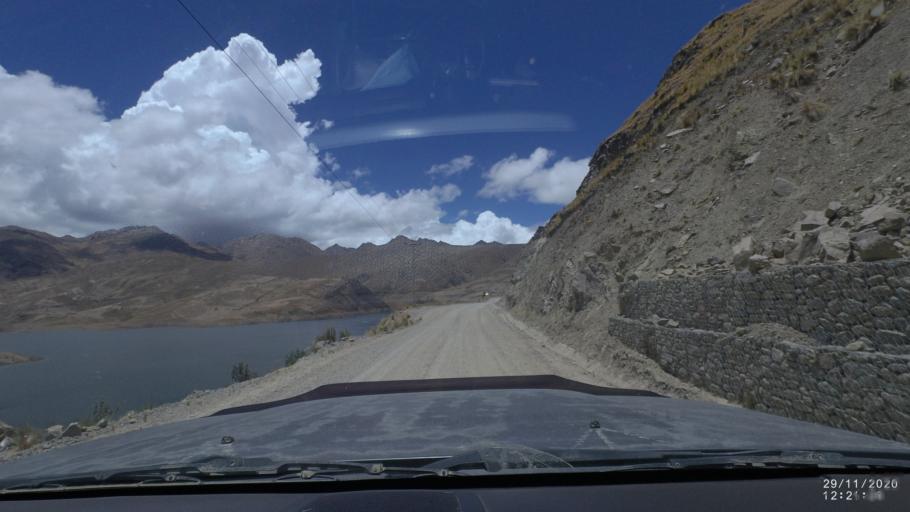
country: BO
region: Cochabamba
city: Cochabamba
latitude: -17.0987
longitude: -66.3225
